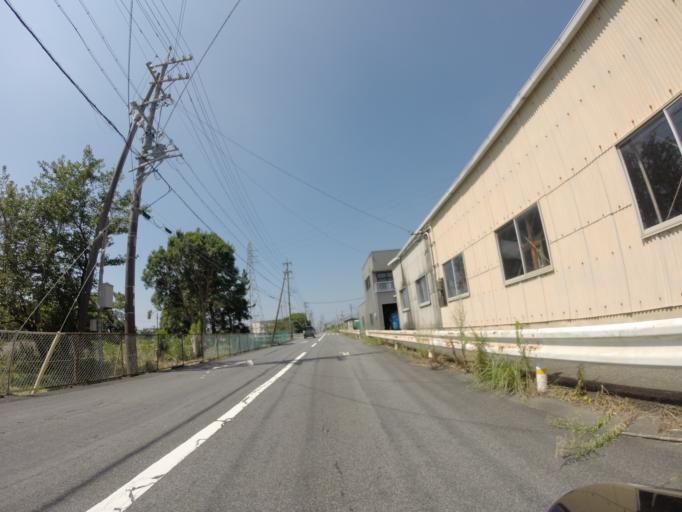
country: JP
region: Shizuoka
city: Fuji
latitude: 35.1252
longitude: 138.6169
